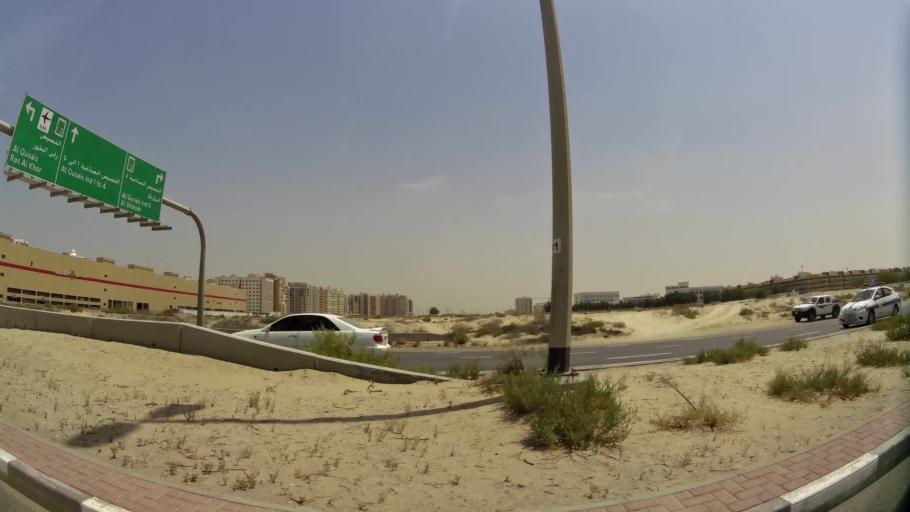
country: AE
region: Ash Shariqah
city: Sharjah
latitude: 25.2794
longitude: 55.3989
